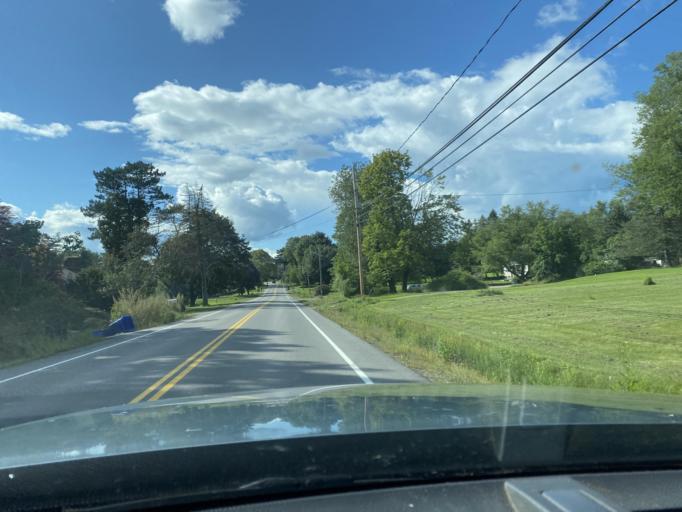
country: US
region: Maine
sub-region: York County
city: Kittery Point
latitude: 43.1448
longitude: -70.7089
